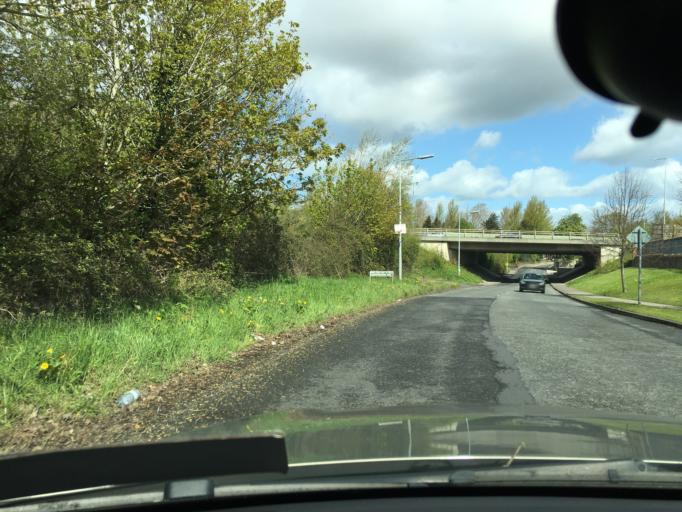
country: IE
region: Leinster
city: Castleknock
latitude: 53.3695
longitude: -6.3763
